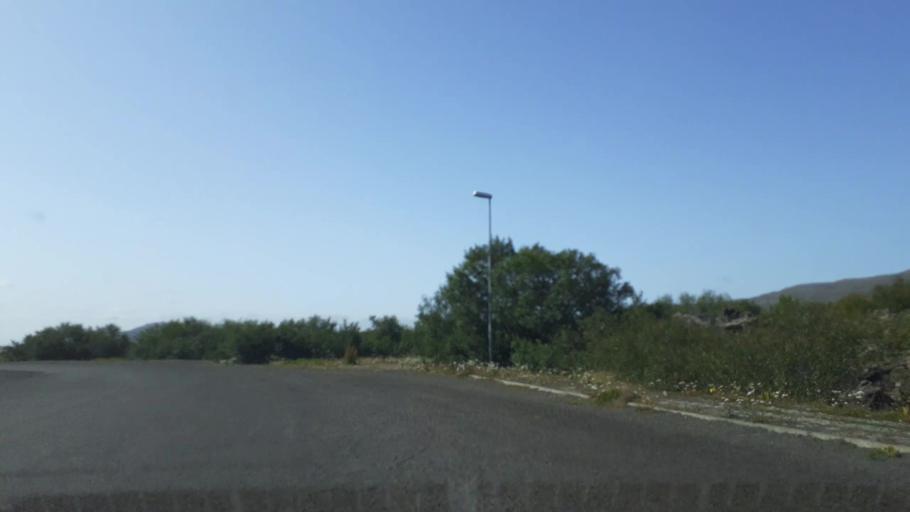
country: IS
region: West
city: Borgarnes
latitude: 64.7663
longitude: -21.5541
